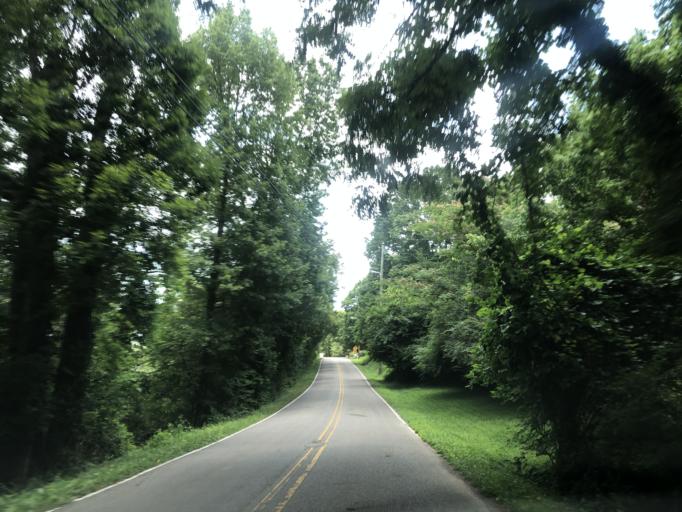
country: US
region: Tennessee
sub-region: Rutherford County
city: La Vergne
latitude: 36.1049
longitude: -86.6500
